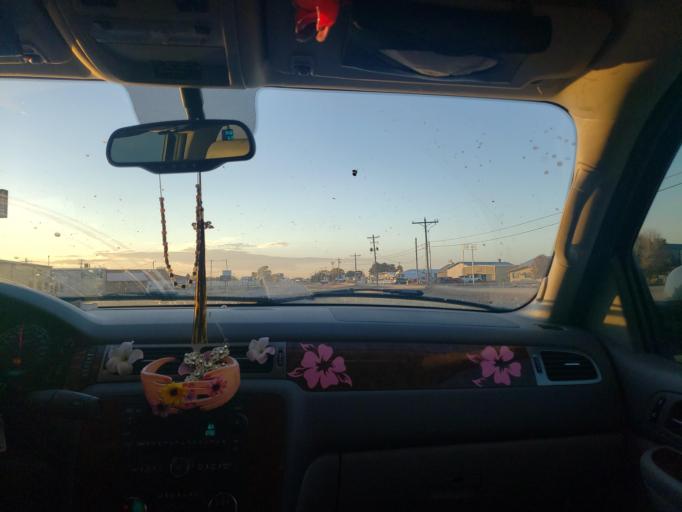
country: US
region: Kansas
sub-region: Finney County
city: Garden City
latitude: 37.9792
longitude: -100.8946
